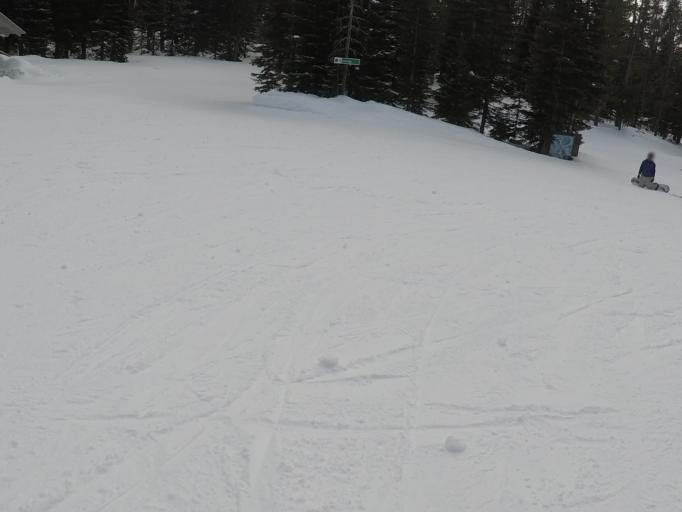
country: US
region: Montana
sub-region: Granite County
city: Philipsburg
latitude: 46.2533
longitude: -113.2206
